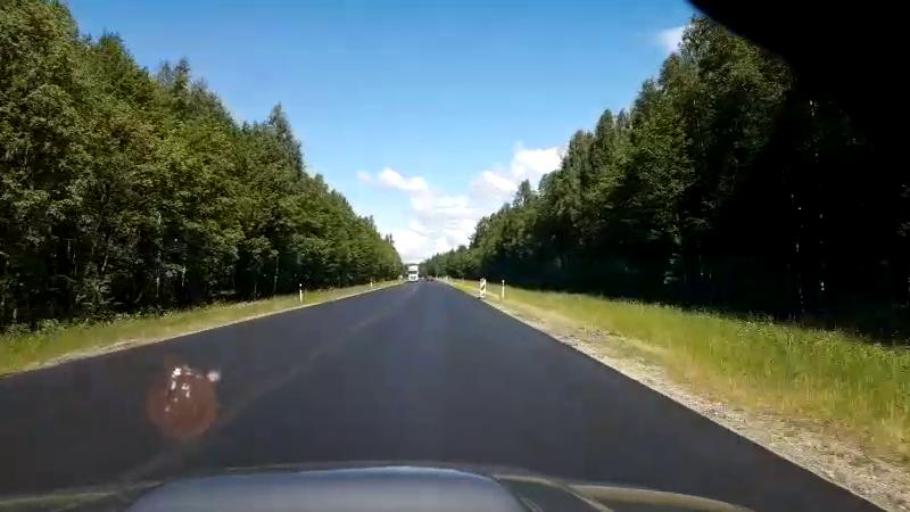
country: LV
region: Salacgrivas
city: Ainazi
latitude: 58.0222
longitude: 24.5000
